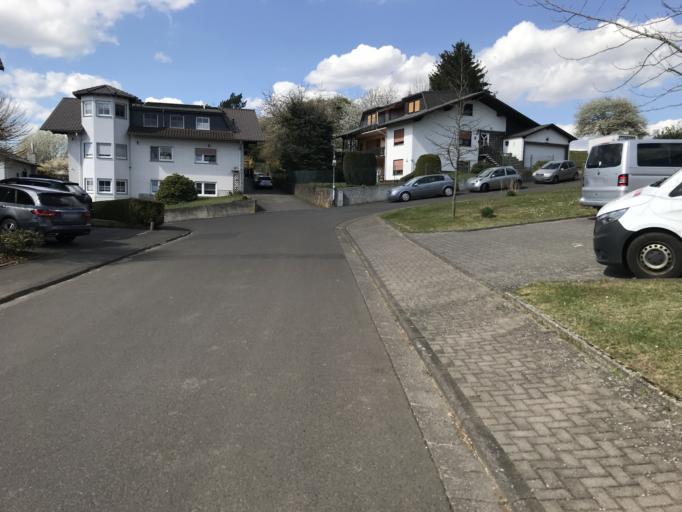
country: DE
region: Hesse
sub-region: Regierungsbezirk Giessen
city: Rabenau
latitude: 50.6949
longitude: 8.8371
